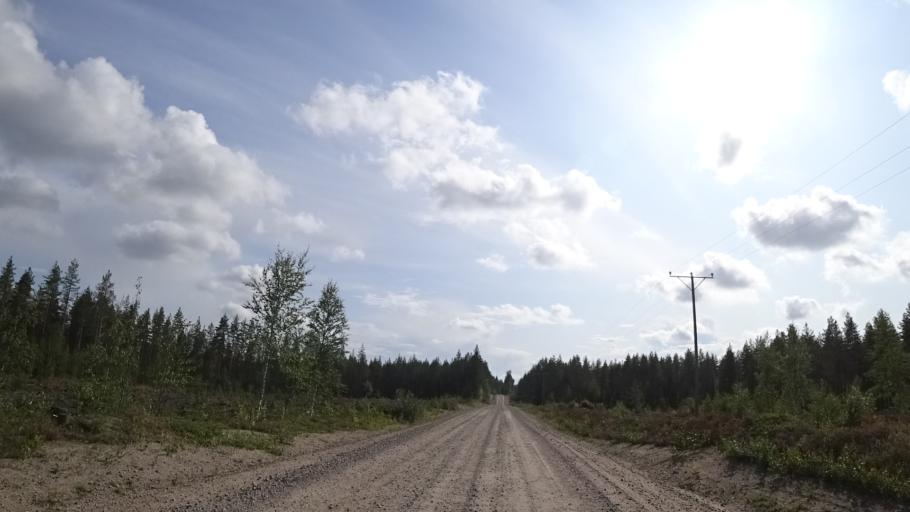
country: FI
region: North Karelia
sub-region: Pielisen Karjala
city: Lieksa
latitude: 63.5603
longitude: 30.0672
